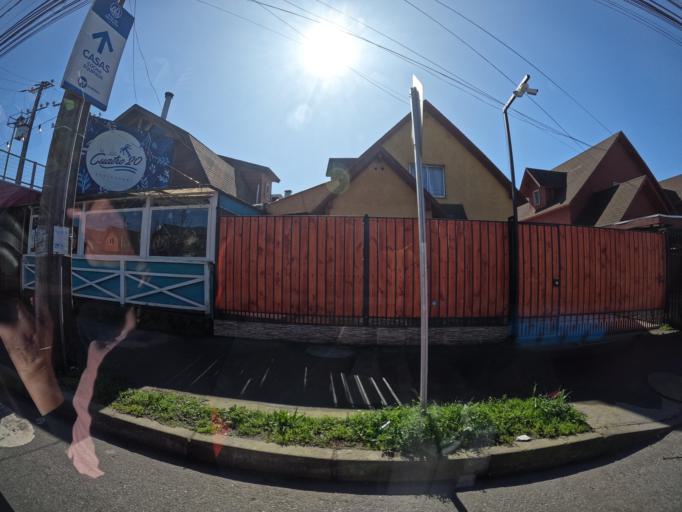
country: CL
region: Biobio
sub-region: Provincia de Concepcion
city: Concepcion
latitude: -36.8822
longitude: -73.1443
